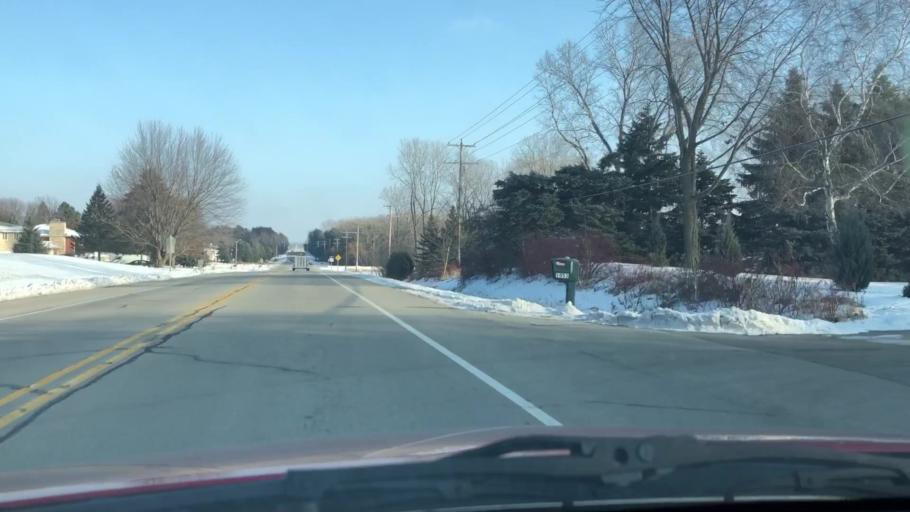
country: US
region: Wisconsin
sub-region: Outagamie County
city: Appleton
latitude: 44.3164
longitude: -88.3889
